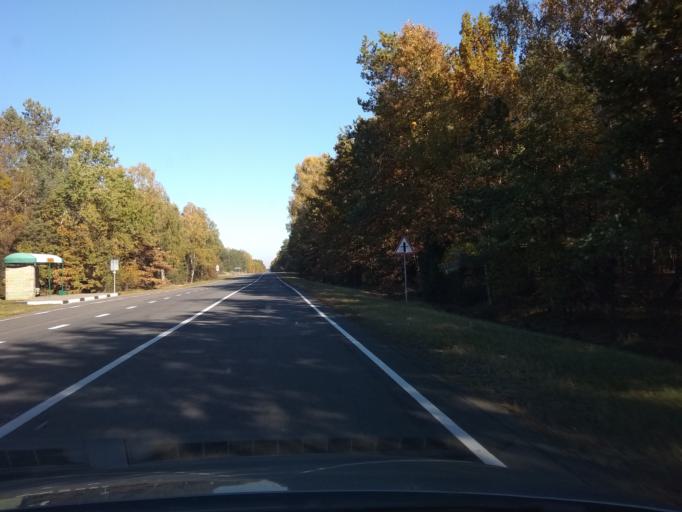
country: BY
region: Brest
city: Kobryn
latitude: 52.0350
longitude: 24.2707
